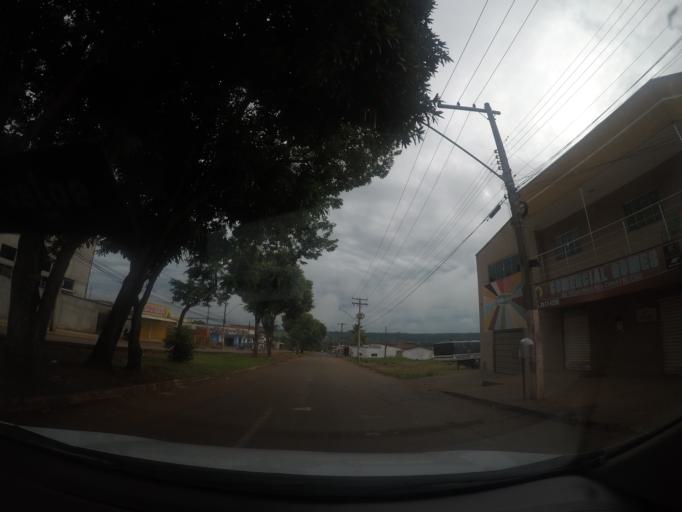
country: BR
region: Goias
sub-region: Goiania
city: Goiania
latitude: -16.5991
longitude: -49.3051
